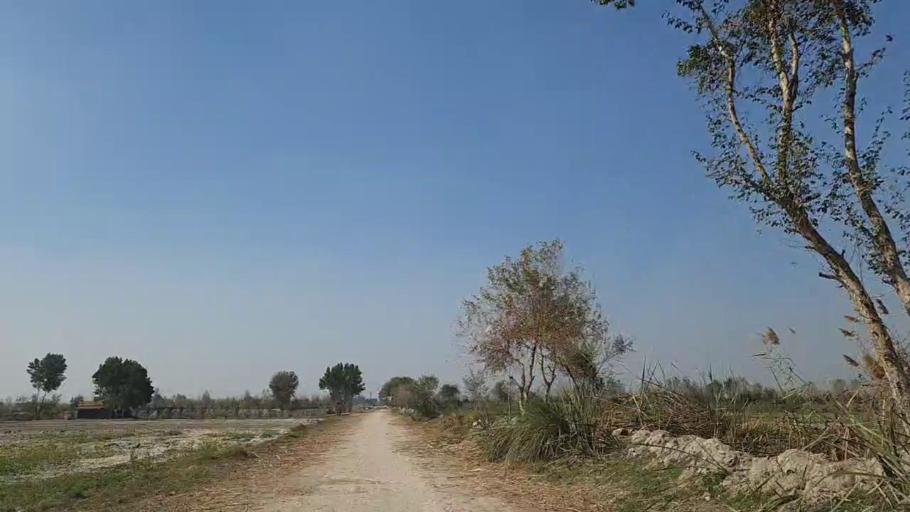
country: PK
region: Sindh
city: Daur
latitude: 26.5001
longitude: 68.3543
